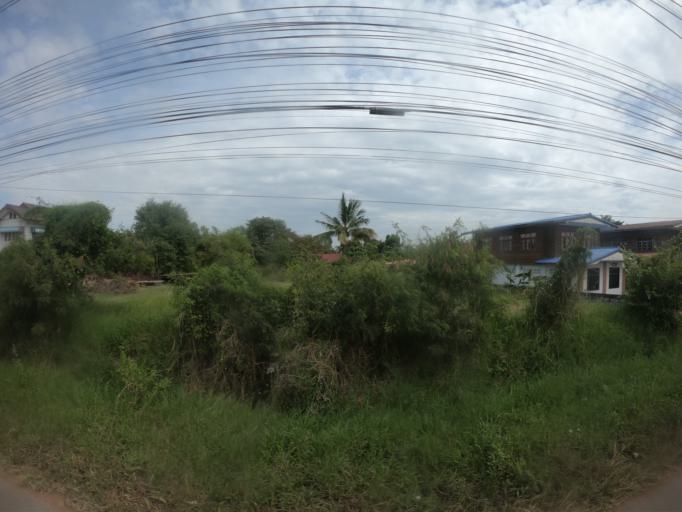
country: TH
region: Maha Sarakham
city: Chiang Yuen
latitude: 16.3502
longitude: 103.1200
